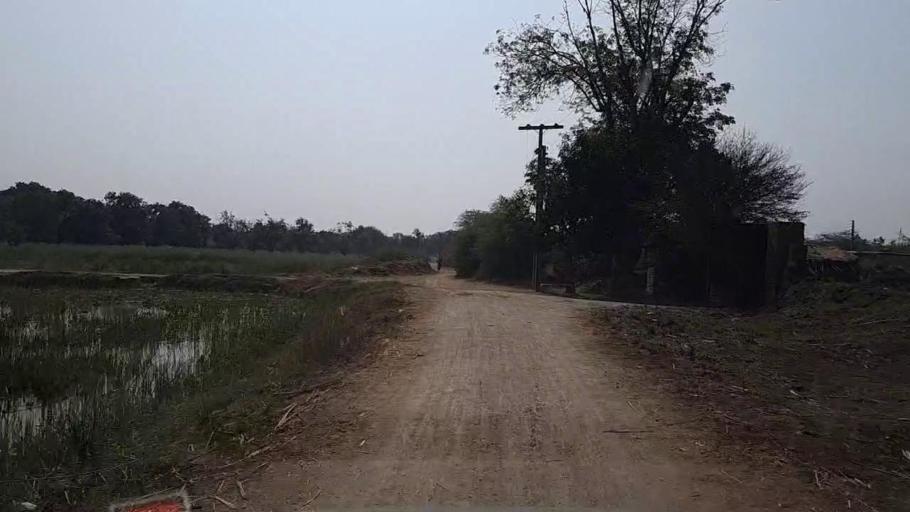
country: PK
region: Sindh
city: Mirwah Gorchani
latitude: 25.3183
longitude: 68.9924
